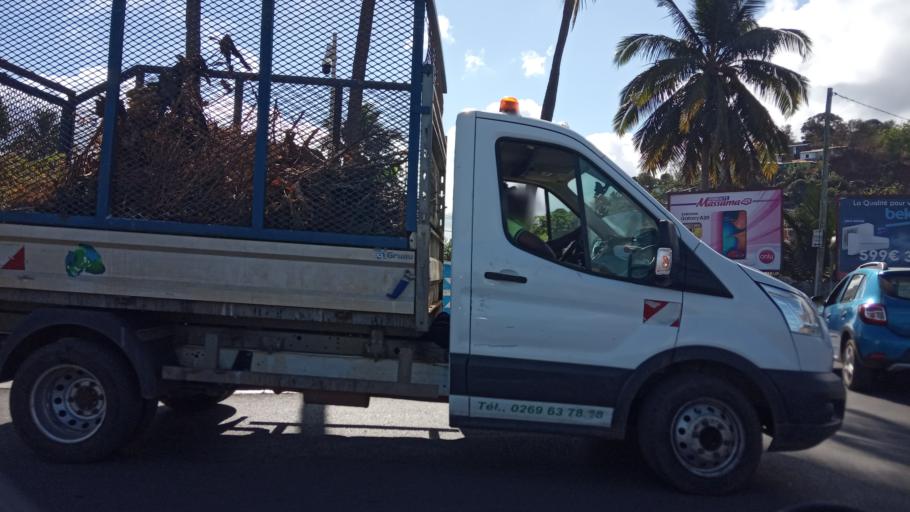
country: YT
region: Mamoudzou
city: Mamoudzou
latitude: -12.7945
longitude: 45.2167
